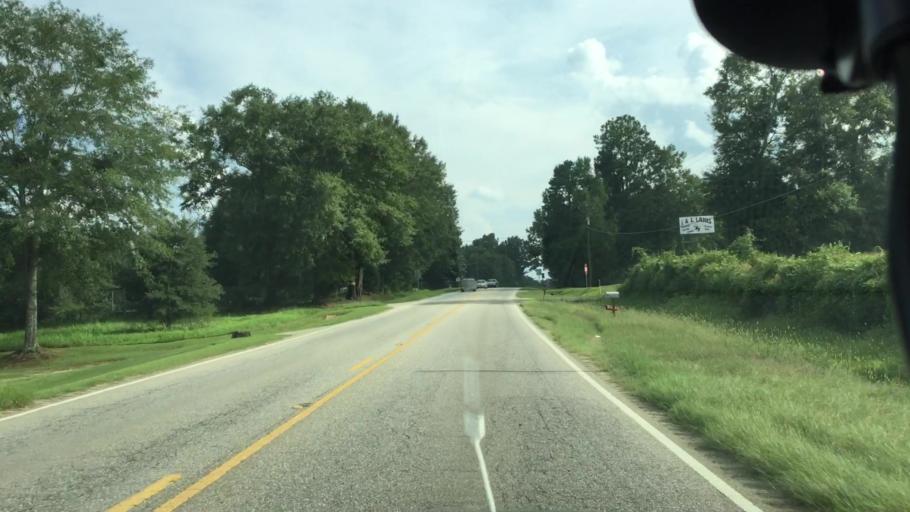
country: US
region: Alabama
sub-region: Pike County
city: Troy
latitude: 31.6964
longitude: -85.9593
